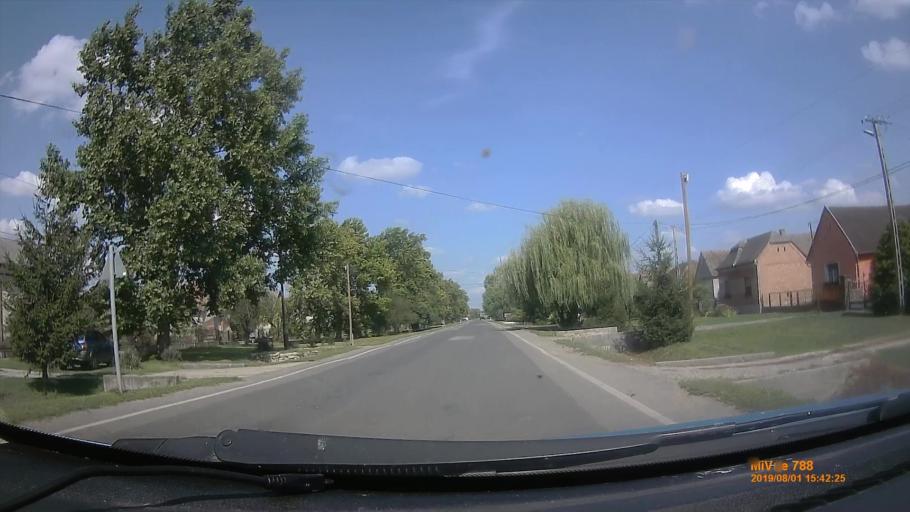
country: HU
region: Baranya
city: Szentlorinc
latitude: 45.9963
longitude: 17.9630
